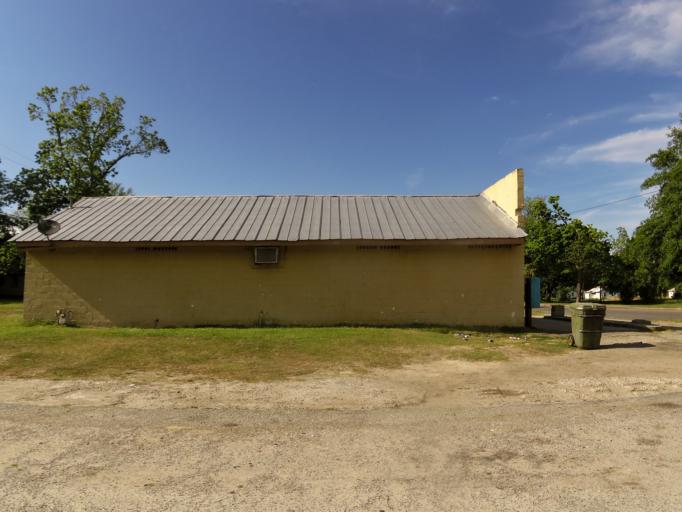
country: US
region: South Carolina
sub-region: Allendale County
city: Fairfax
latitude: 32.9521
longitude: -81.2361
